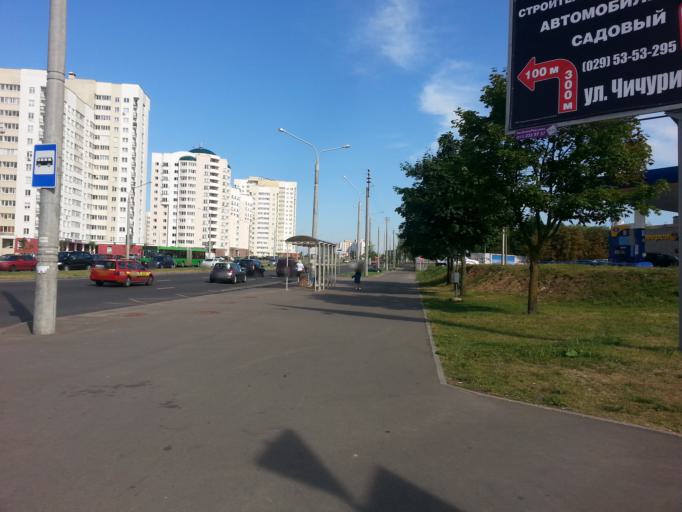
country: BY
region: Minsk
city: Novoye Medvezhino
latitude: 53.9169
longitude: 27.4562
